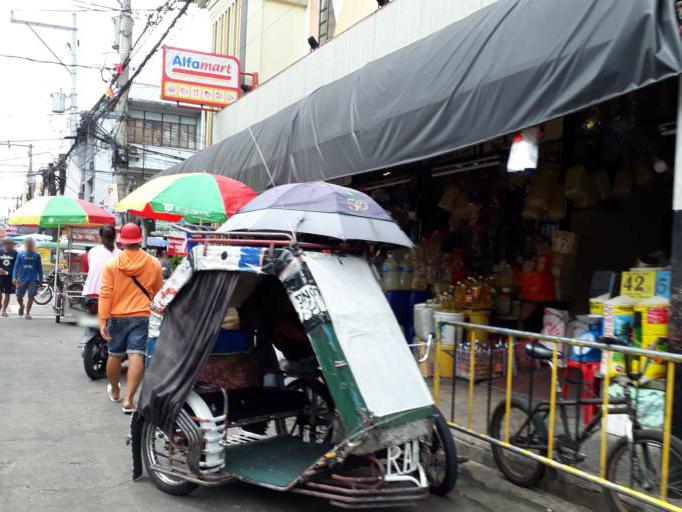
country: PH
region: Metro Manila
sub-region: City of Manila
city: Manila
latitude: 14.6099
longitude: 120.9958
